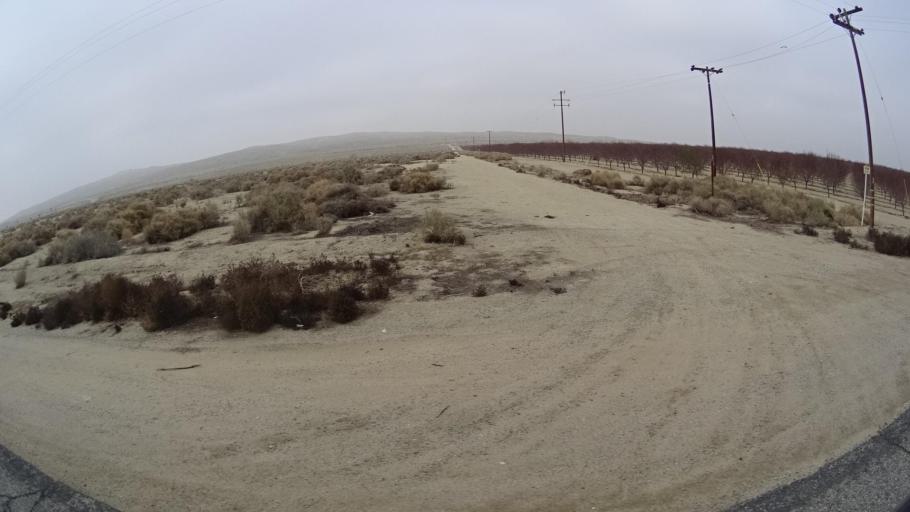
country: US
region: California
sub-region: Kern County
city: Maricopa
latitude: 35.1231
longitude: -119.3588
